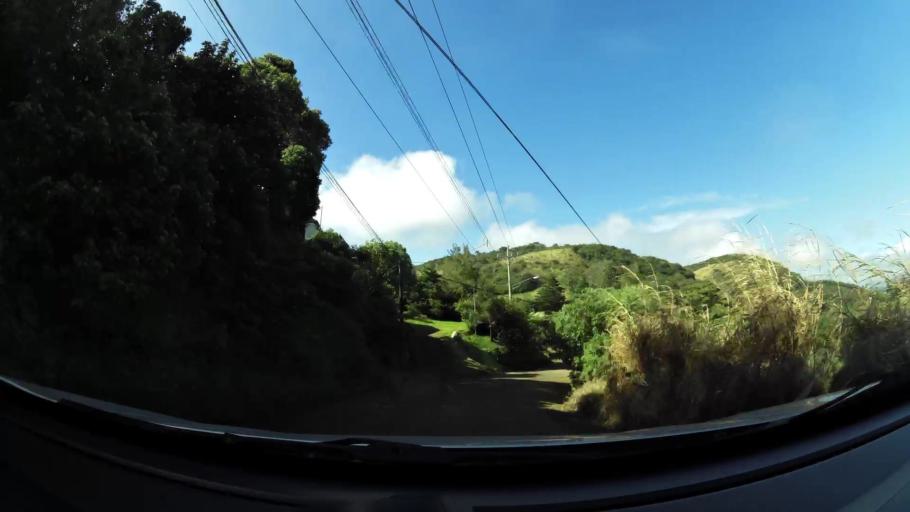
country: CR
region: Guanacaste
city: Juntas
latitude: 10.3290
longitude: -84.8427
